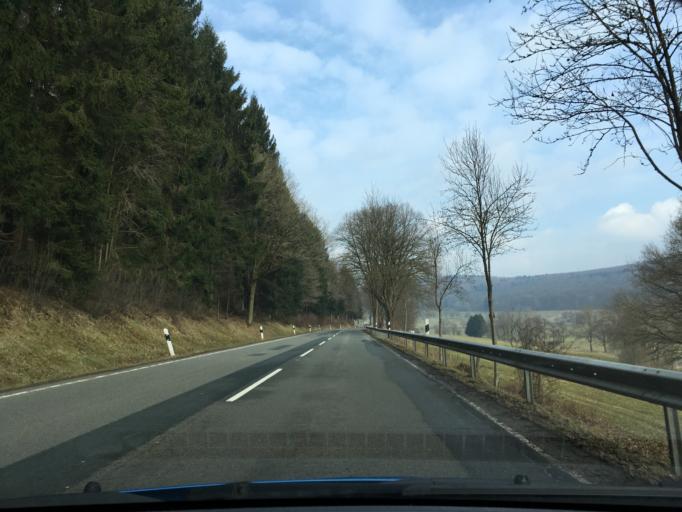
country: DE
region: Lower Saxony
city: Bodenfelde
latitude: 51.7024
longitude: 9.5481
